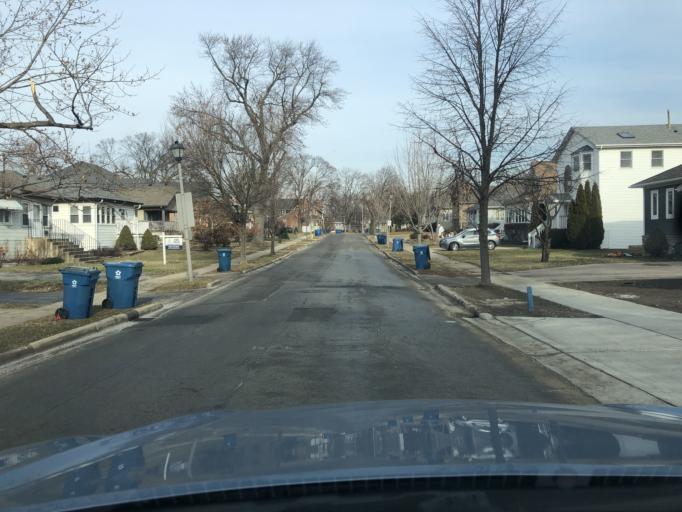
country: US
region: Illinois
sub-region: DuPage County
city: Elmhurst
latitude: 41.9048
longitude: -87.9293
